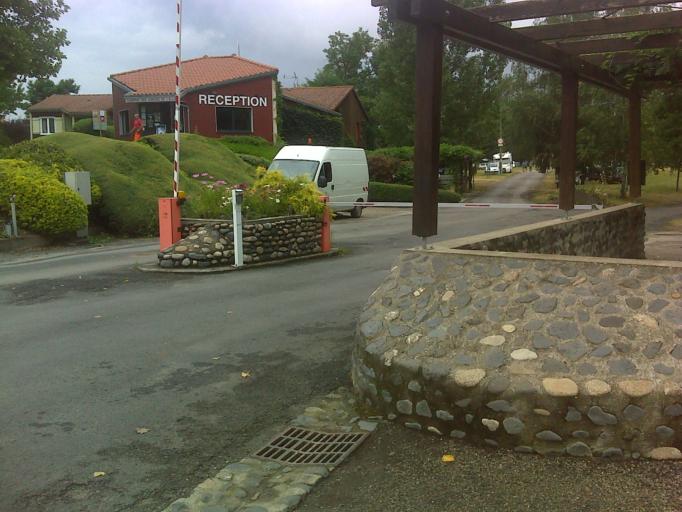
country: FR
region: Auvergne
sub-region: Departement de la Haute-Loire
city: Langeac
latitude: 45.1023
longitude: 3.4996
